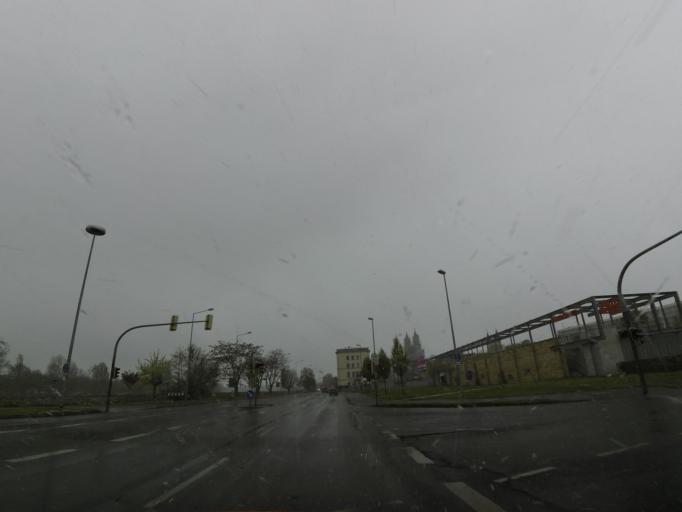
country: DE
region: Saxony-Anhalt
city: Magdeburg
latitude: 52.1290
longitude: 11.6420
